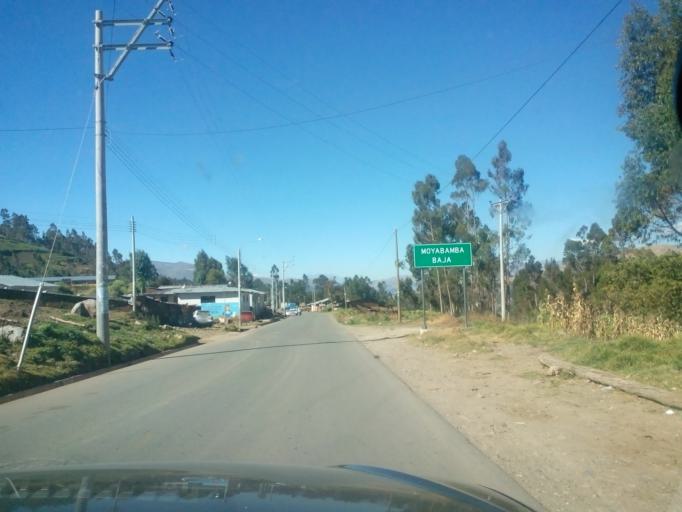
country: PE
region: Apurimac
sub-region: Provincia de Andahuaylas
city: Talavera
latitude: -13.6519
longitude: -73.5246
